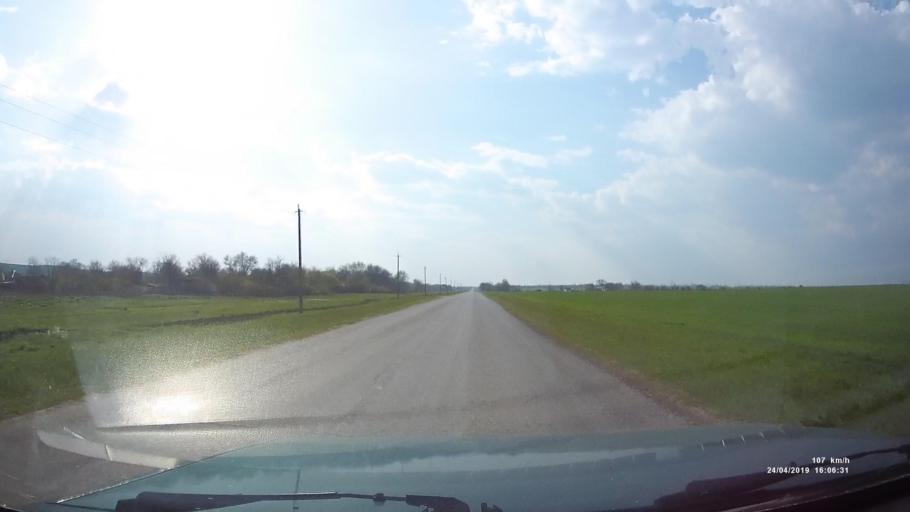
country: RU
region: Rostov
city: Sovetskoye
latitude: 46.6870
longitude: 42.3474
